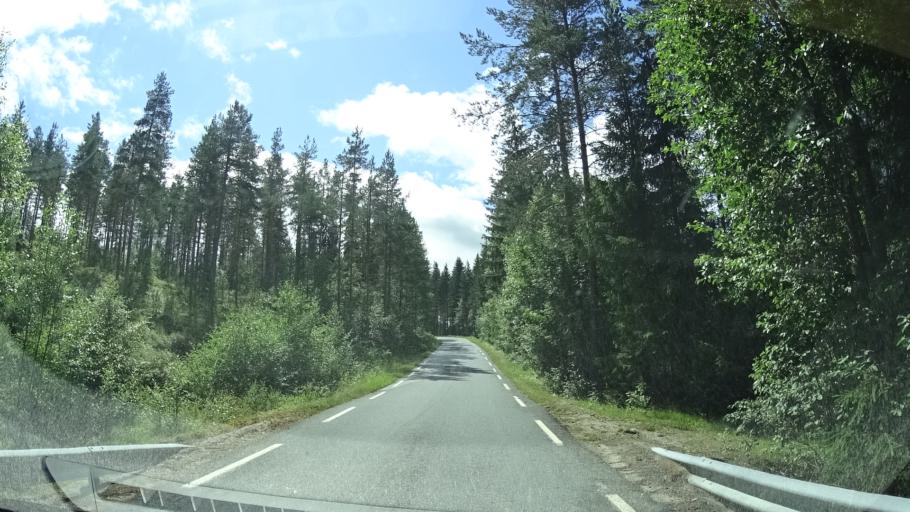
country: NO
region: Buskerud
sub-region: Krodsherad
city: Noresund
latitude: 60.2263
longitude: 9.8333
